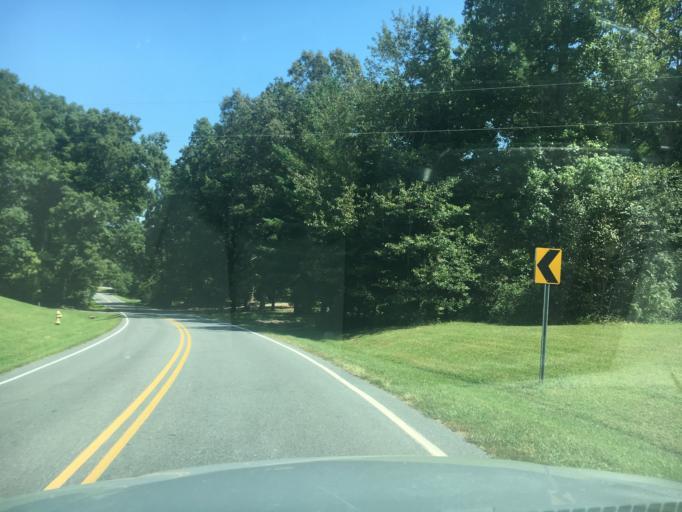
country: US
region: North Carolina
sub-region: Rutherford County
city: Forest City
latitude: 35.3027
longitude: -81.8926
